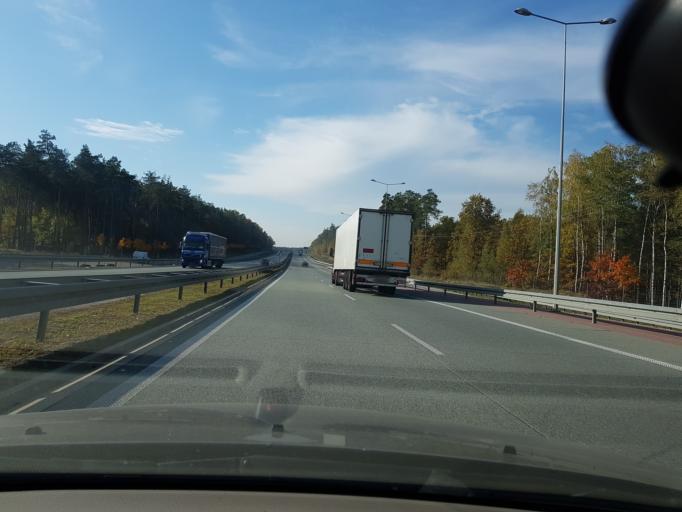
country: PL
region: Lodz Voivodeship
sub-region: Powiat tomaszowski
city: Lubochnia
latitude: 51.5882
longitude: 20.0395
